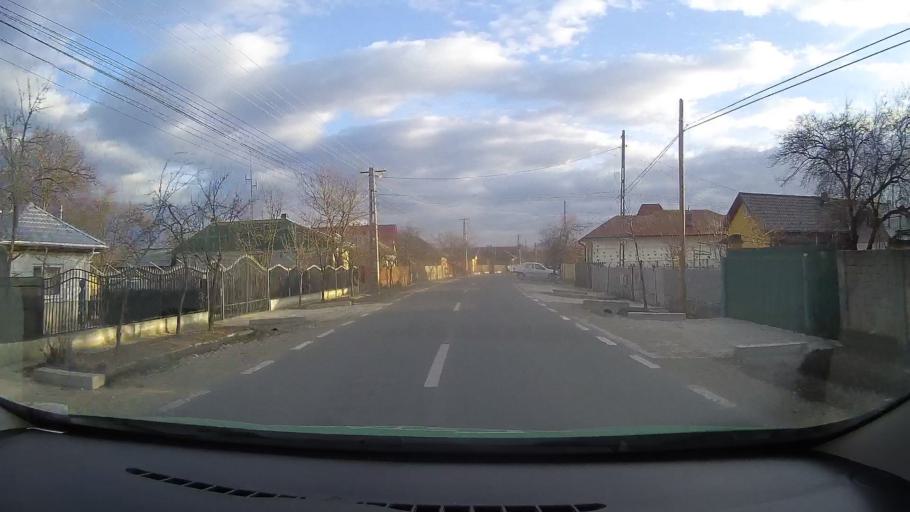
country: RO
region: Dambovita
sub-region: Comuna I. L. Caragiale
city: Ghirdoveni
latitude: 44.9516
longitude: 25.6582
